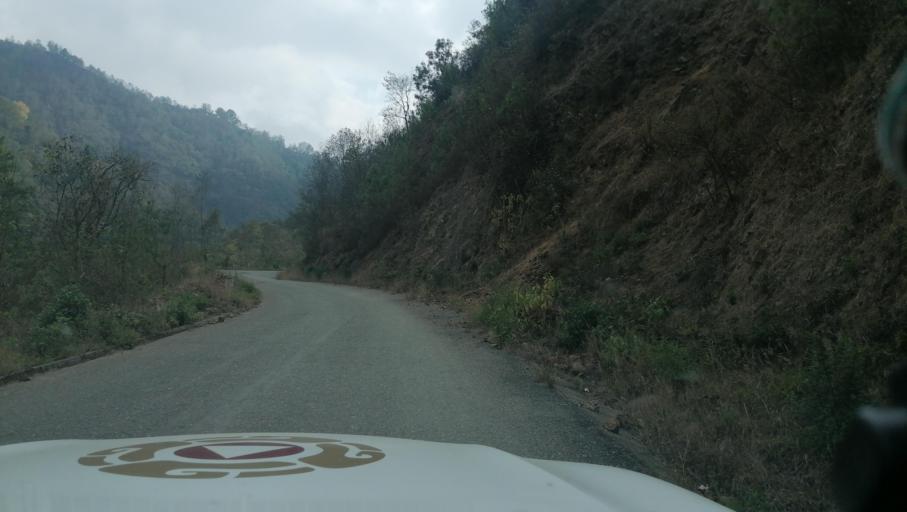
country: GT
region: San Marcos
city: Tacana
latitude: 15.2273
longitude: -92.1943
